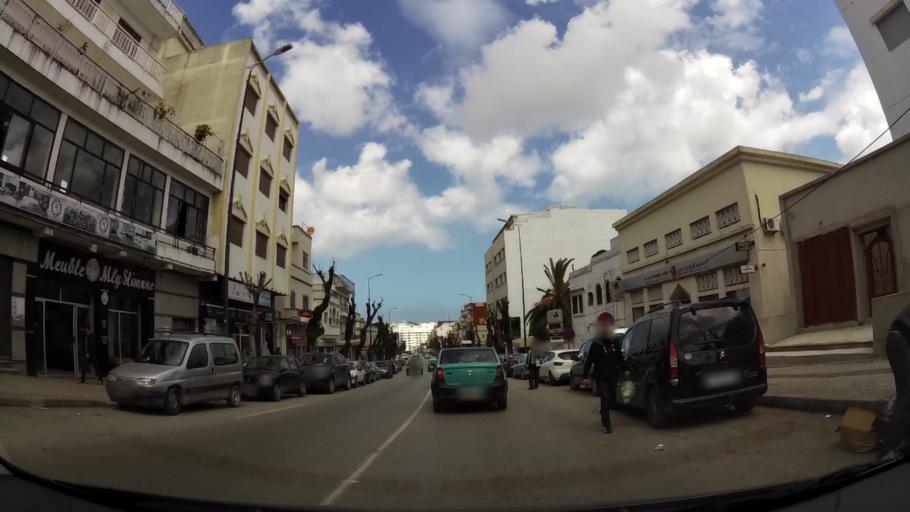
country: MA
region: Tanger-Tetouan
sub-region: Tanger-Assilah
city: Tangier
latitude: 35.7599
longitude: -5.8128
